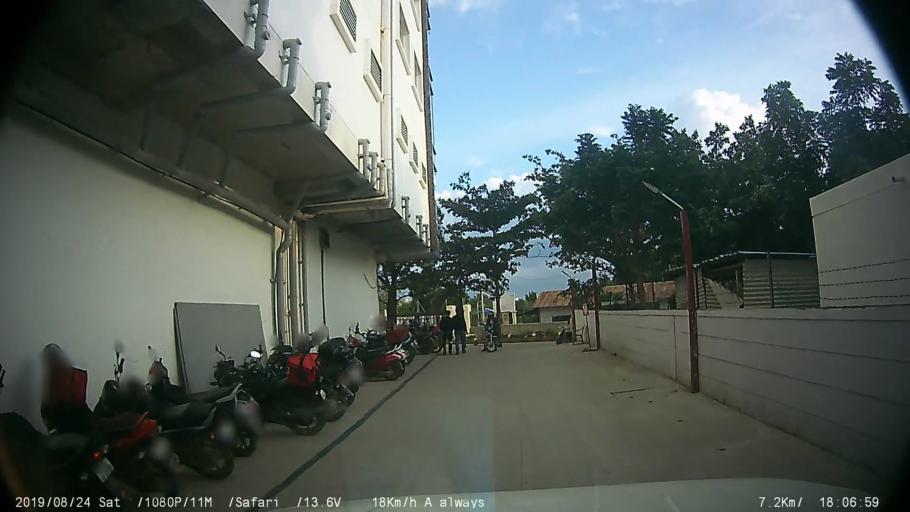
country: IN
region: Karnataka
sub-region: Bangalore Urban
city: Anekal
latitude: 12.8404
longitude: 77.6533
